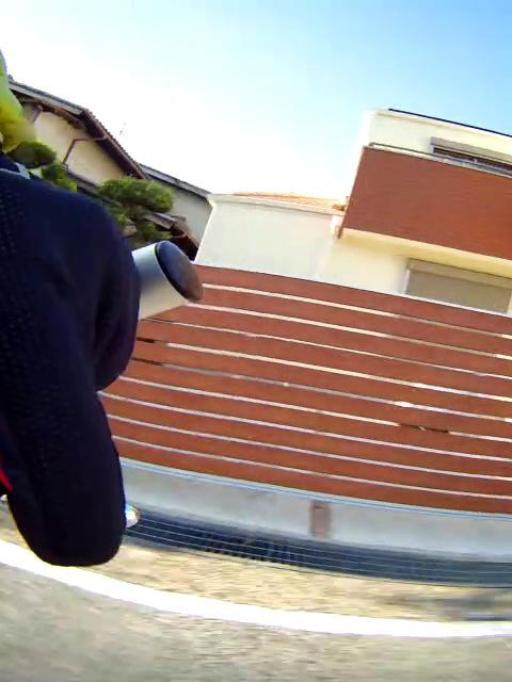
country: JP
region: Hyogo
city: Takarazuka
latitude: 34.7923
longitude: 135.3439
